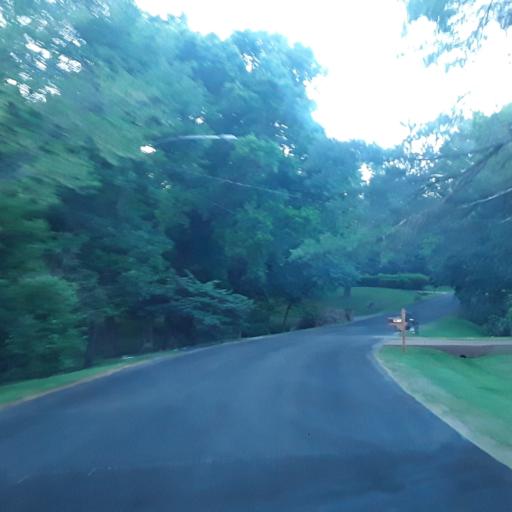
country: US
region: Tennessee
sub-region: Davidson County
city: Oak Hill
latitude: 36.0646
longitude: -86.7661
